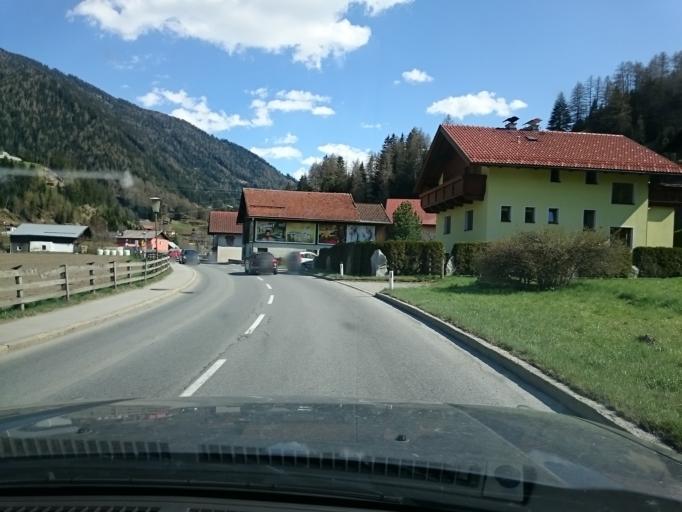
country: AT
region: Tyrol
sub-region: Politischer Bezirk Innsbruck Land
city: Steinach am Brenner
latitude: 47.0852
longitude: 11.4695
